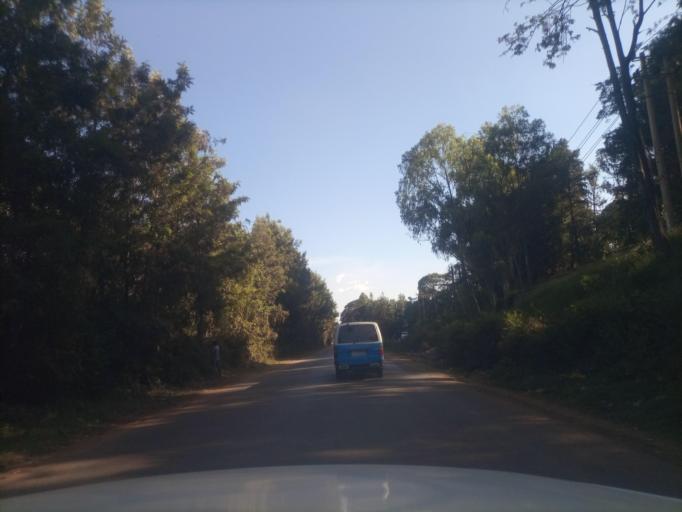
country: ET
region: Oromiya
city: Jima
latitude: 7.6842
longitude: 36.8328
